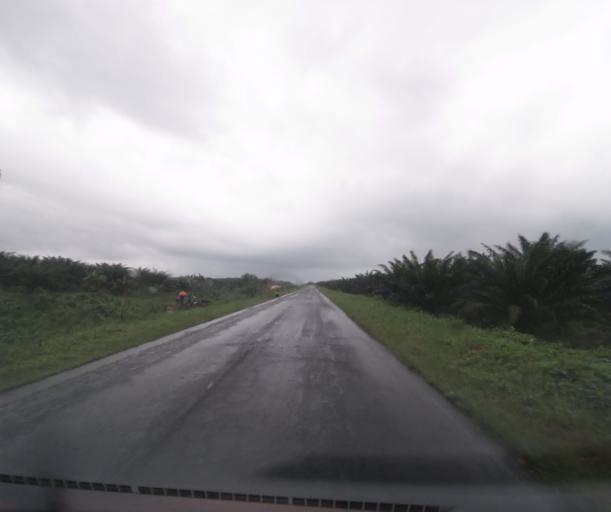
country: CM
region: South-West Province
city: Idenao
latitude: 4.1567
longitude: 8.9924
